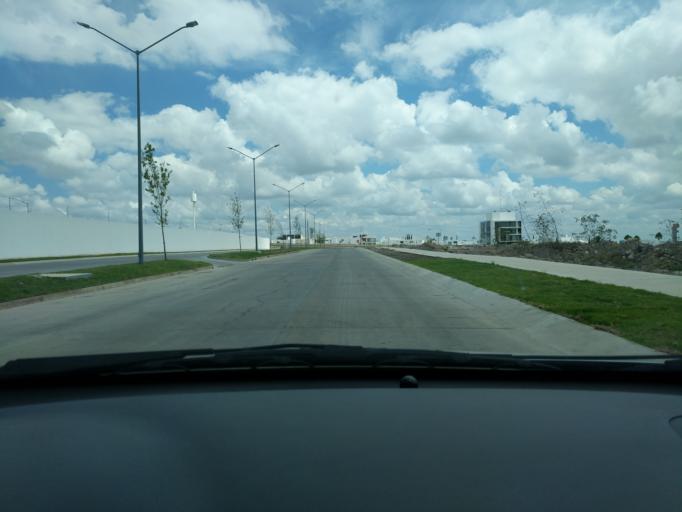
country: MX
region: San Luis Potosi
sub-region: Mexquitic de Carmona
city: Guadalupe Victoria
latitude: 22.1658
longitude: -101.0456
